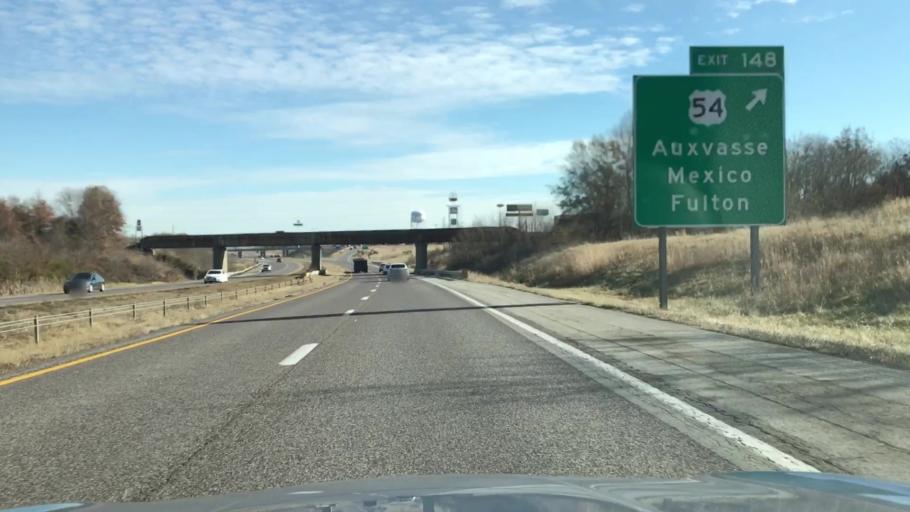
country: US
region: Missouri
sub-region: Callaway County
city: Fulton
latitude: 38.9448
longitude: -91.9490
